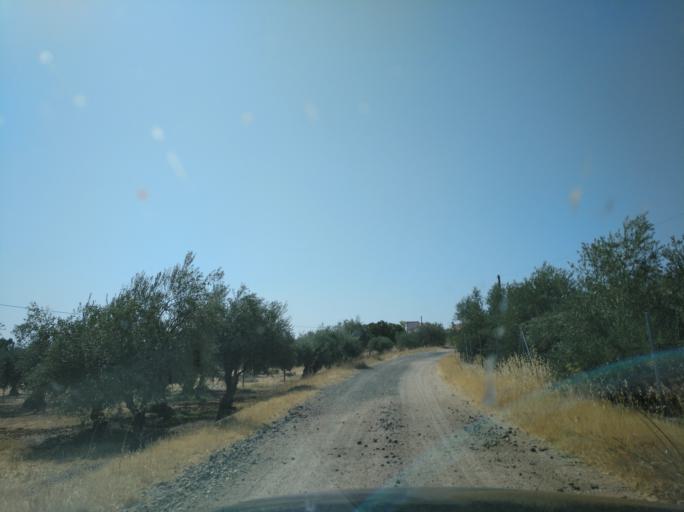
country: PT
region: Portalegre
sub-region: Campo Maior
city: Campo Maior
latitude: 39.0728
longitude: -7.0169
